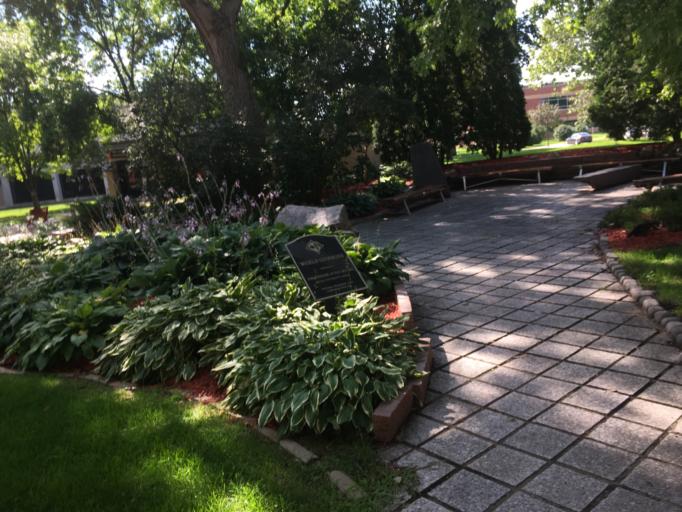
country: US
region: Minnesota
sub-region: Stearns County
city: Saint Cloud
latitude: 45.5527
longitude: -94.1509
